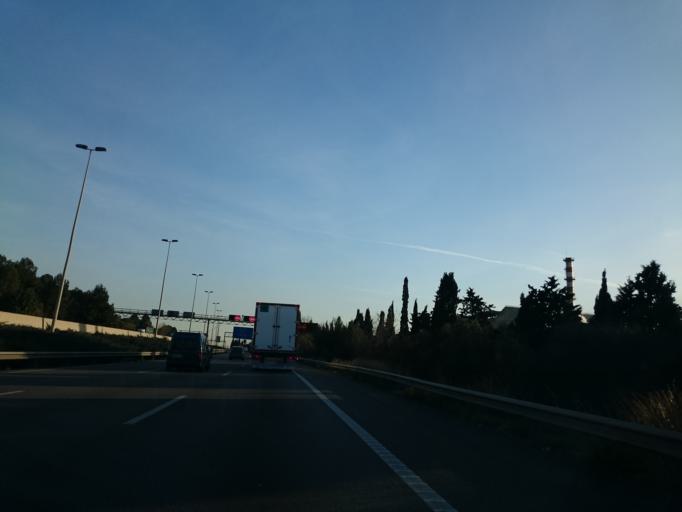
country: ES
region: Catalonia
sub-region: Provincia de Barcelona
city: Sant Andreu de la Barca
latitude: 41.4573
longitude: 1.9816
